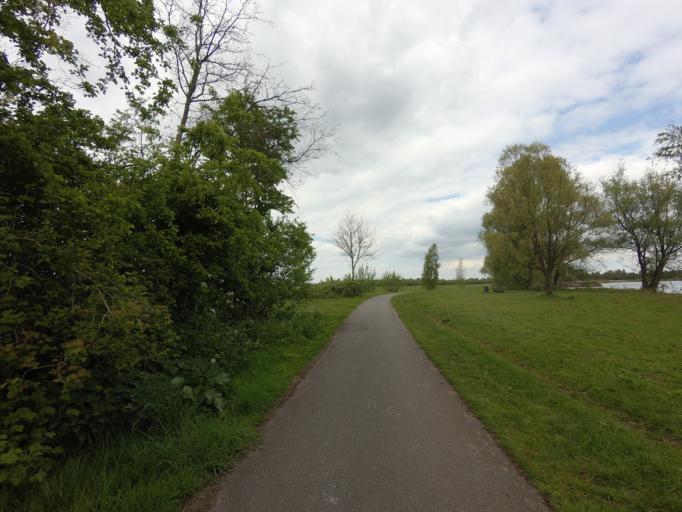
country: NL
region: Utrecht
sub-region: Gemeente De Bilt
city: De Bilt
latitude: 52.1118
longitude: 5.1592
